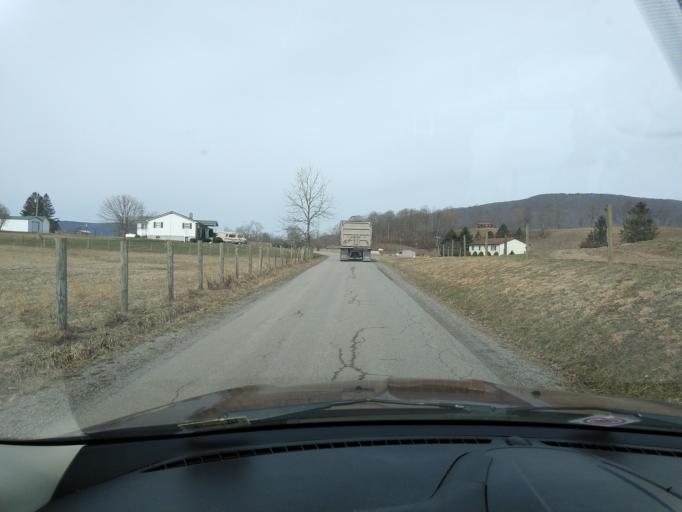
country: US
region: West Virginia
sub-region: Tucker County
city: Parsons
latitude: 39.0216
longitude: -79.5374
